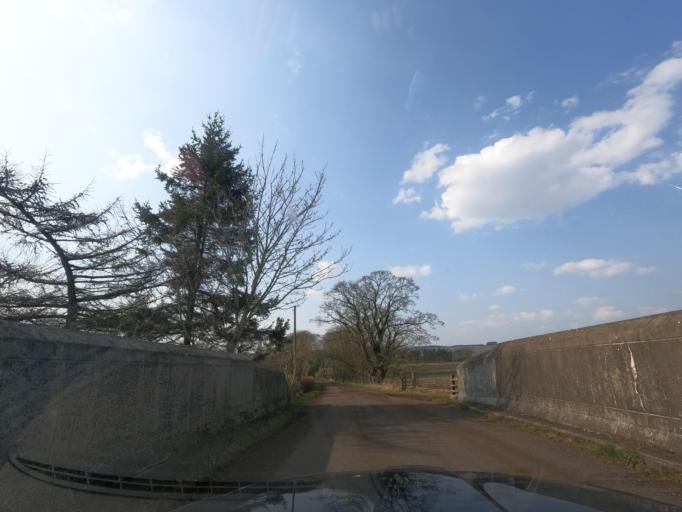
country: GB
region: Scotland
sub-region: South Lanarkshire
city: Carnwath
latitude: 55.7424
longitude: -3.6157
